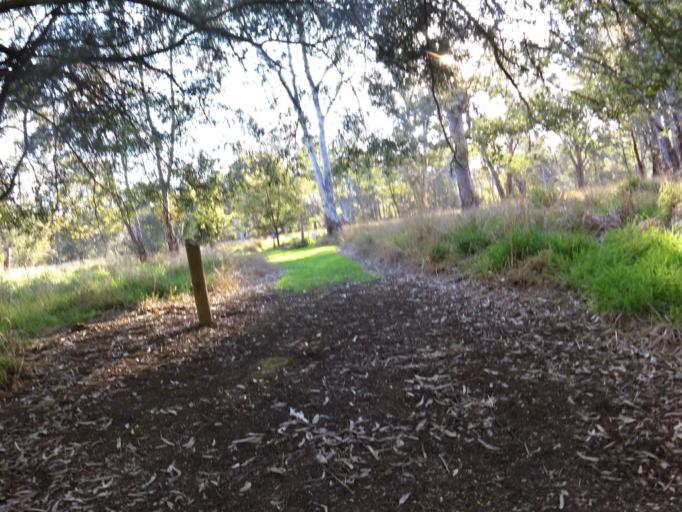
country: AU
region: Victoria
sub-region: Murrindindi
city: Alexandra
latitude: -37.2055
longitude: 145.4267
